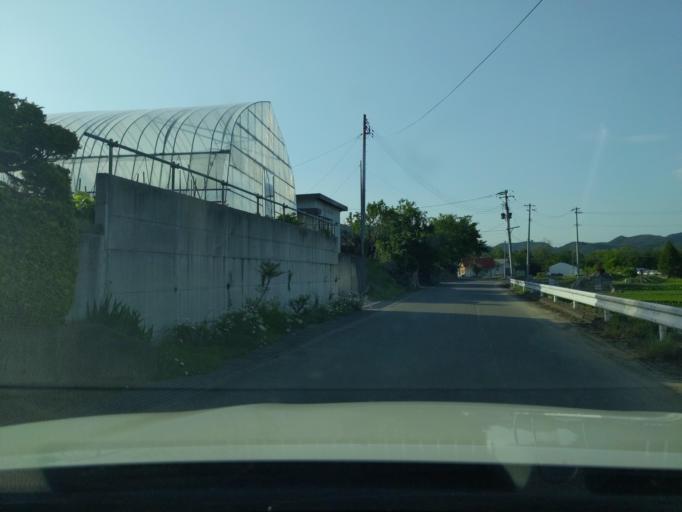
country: JP
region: Fukushima
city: Motomiya
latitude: 37.4699
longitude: 140.3303
